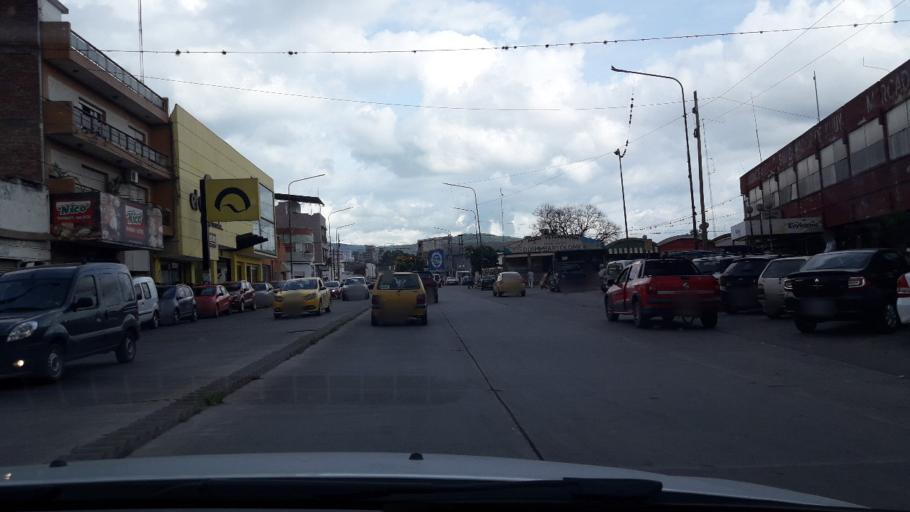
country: AR
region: Jujuy
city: San Salvador de Jujuy
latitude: -24.1937
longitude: -65.2899
